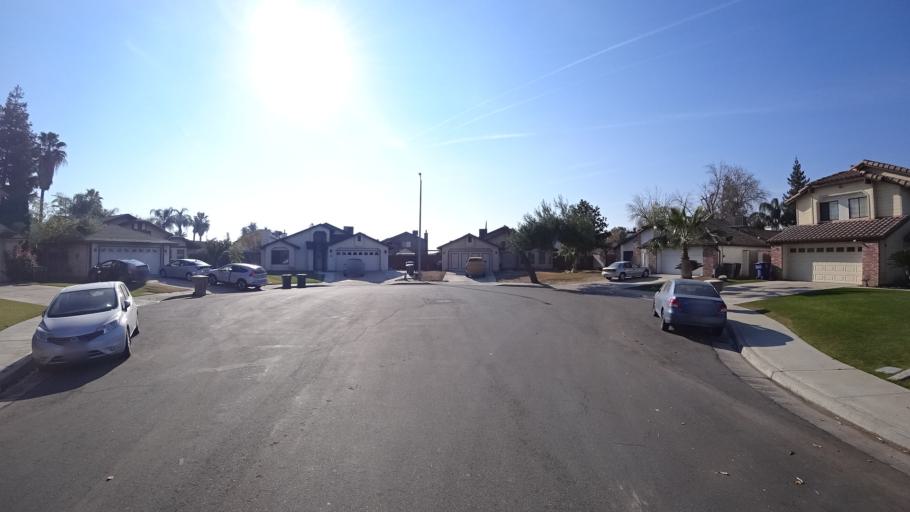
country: US
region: California
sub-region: Kern County
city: Greenfield
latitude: 35.3119
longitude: -119.0275
